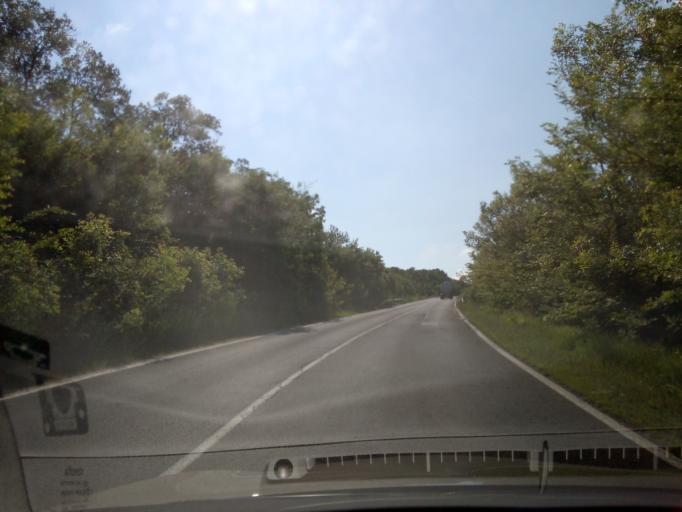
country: BG
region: Burgas
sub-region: Obshtina Nesebur
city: Sveti Vlas
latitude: 42.7483
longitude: 27.7496
